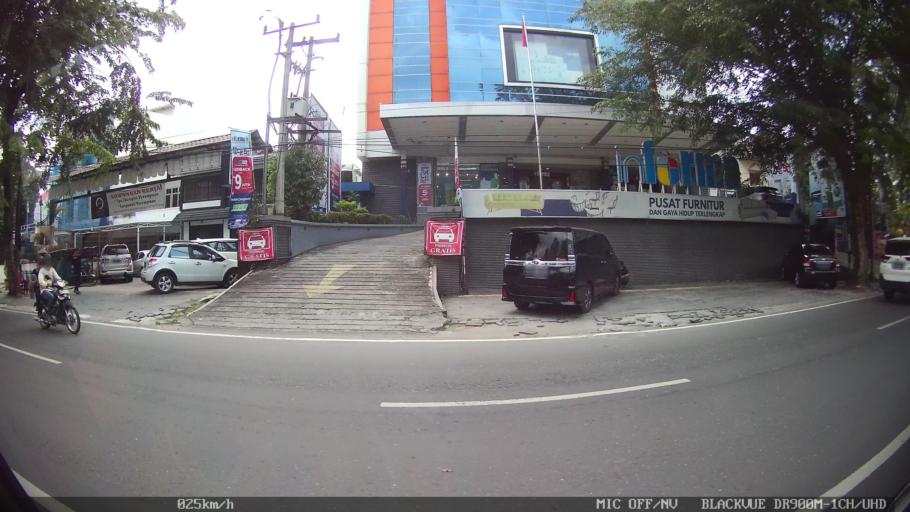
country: ID
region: North Sumatra
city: Medan
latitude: 3.5820
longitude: 98.6671
